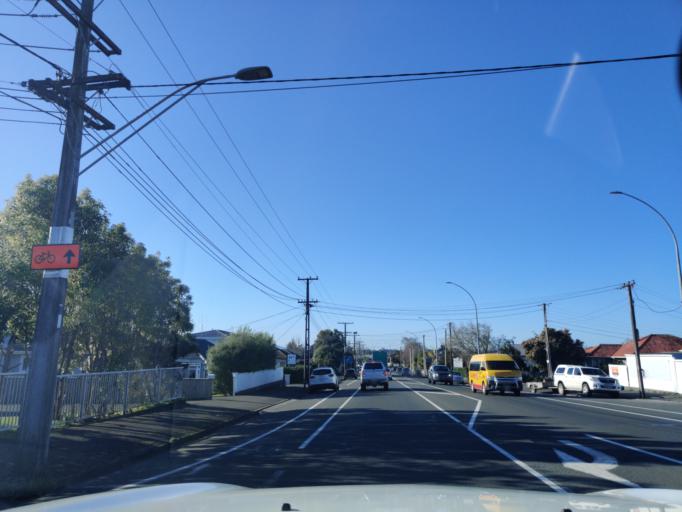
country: NZ
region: Waikato
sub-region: Hamilton City
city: Hamilton
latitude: -37.7995
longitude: 175.3166
